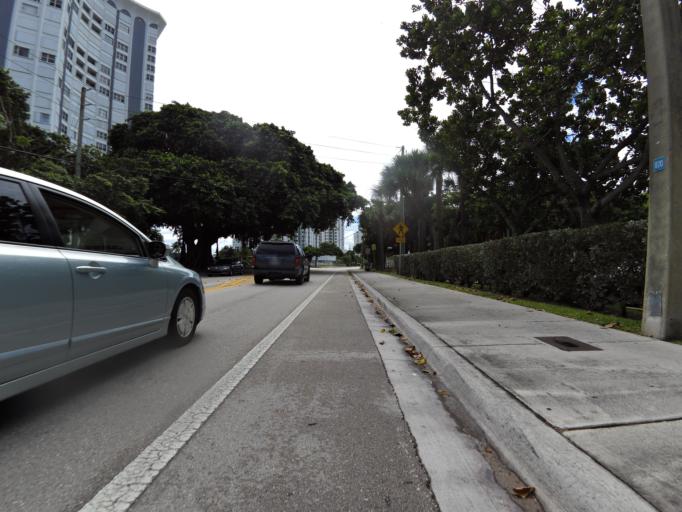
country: US
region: Florida
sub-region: Broward County
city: Terra Mar
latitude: 26.2215
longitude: -80.0913
